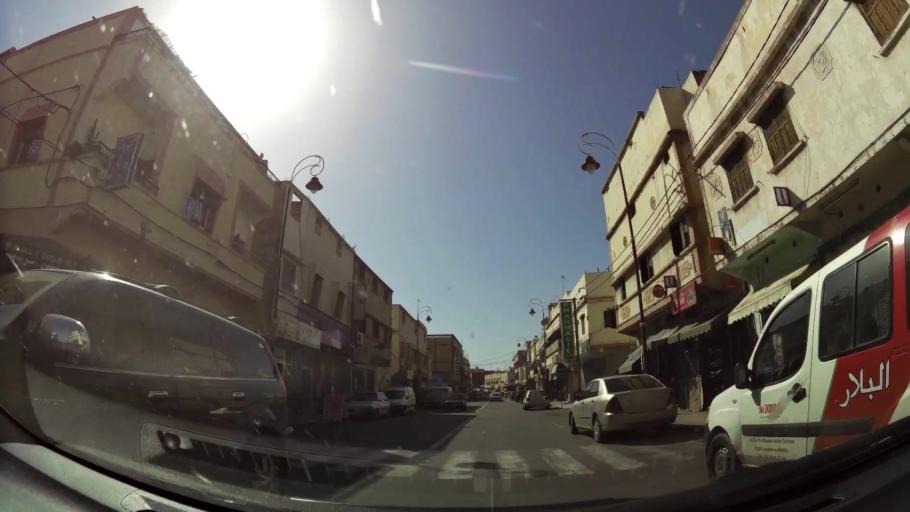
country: MA
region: Souss-Massa-Draa
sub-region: Inezgane-Ait Mellou
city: Inezgane
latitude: 30.3710
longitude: -9.5410
